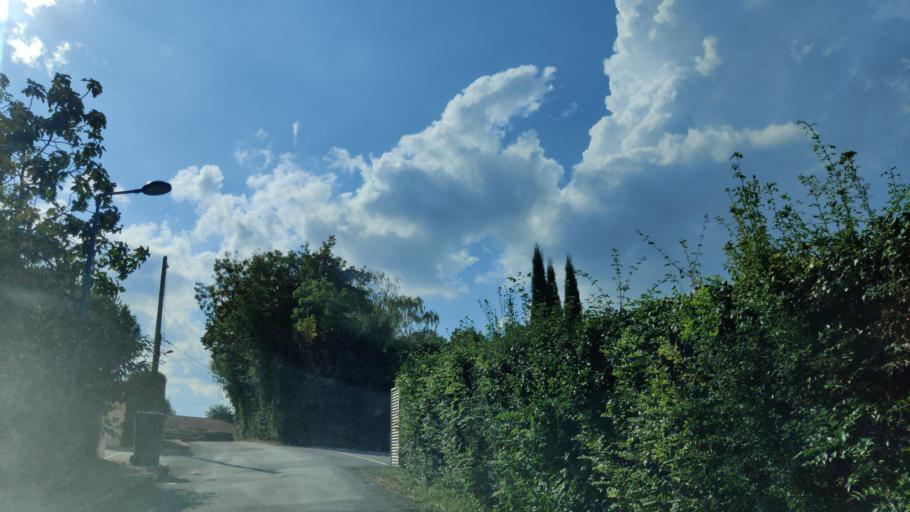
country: FR
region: Poitou-Charentes
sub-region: Departement des Deux-Sevres
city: Bessines
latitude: 46.2998
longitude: -0.5041
